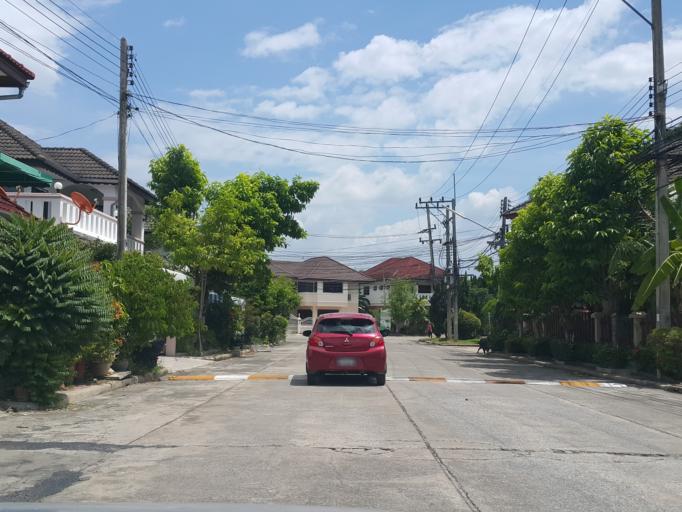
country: TH
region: Chiang Mai
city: Hang Dong
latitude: 18.7378
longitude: 98.9452
